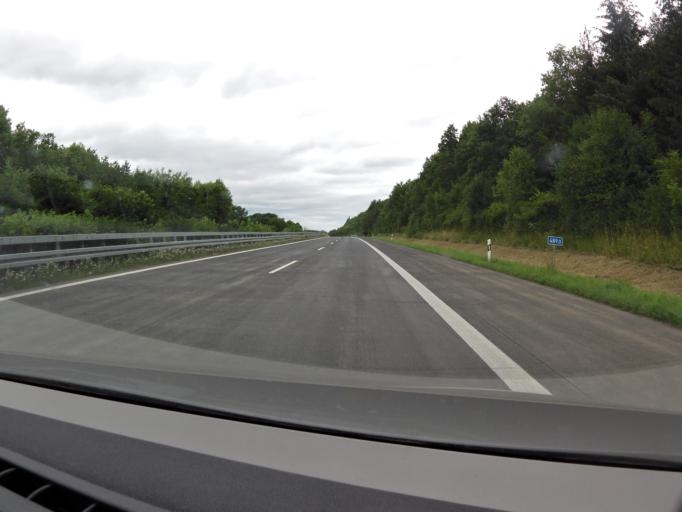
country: DE
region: Baden-Wuerttemberg
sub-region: Regierungsbezirk Stuttgart
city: Buch am Ahorn
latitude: 49.4873
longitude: 9.5656
